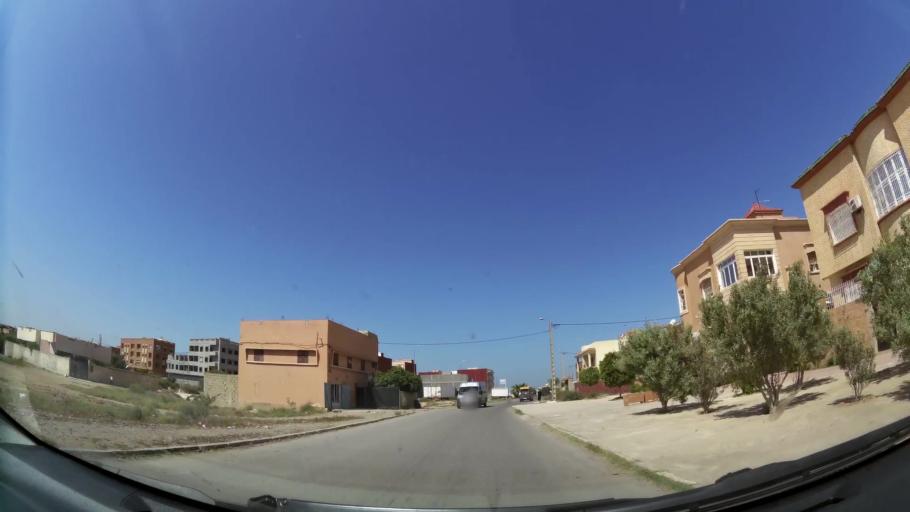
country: MA
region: Souss-Massa-Draa
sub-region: Inezgane-Ait Mellou
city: Inezgane
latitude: 30.3210
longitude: -9.5039
